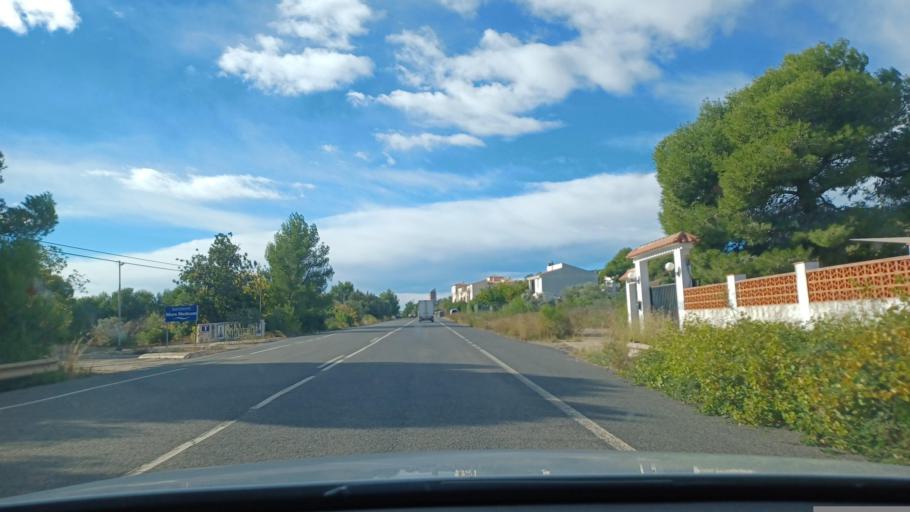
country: ES
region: Catalonia
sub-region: Provincia de Tarragona
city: Sant Carles de la Rapita
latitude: 40.5872
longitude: 0.5600
